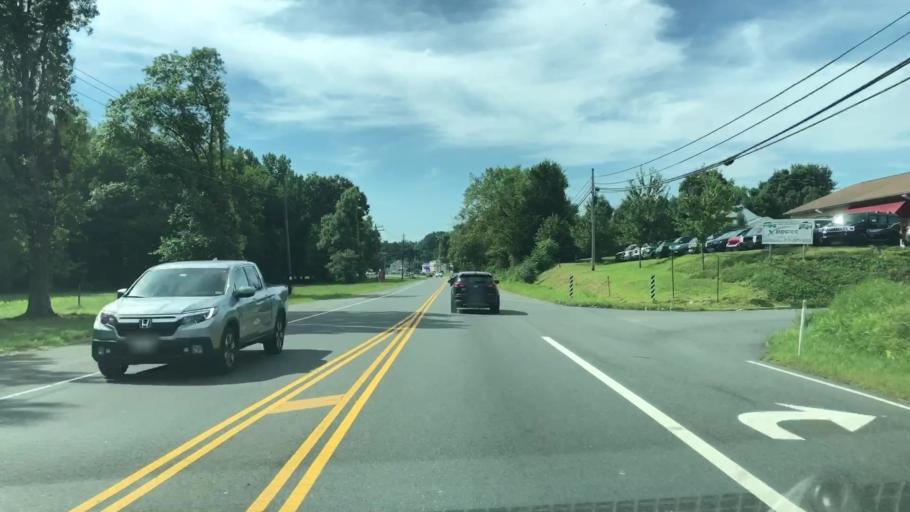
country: US
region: Virginia
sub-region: City of Fredericksburg
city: Fredericksburg
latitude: 38.2810
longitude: -77.4536
